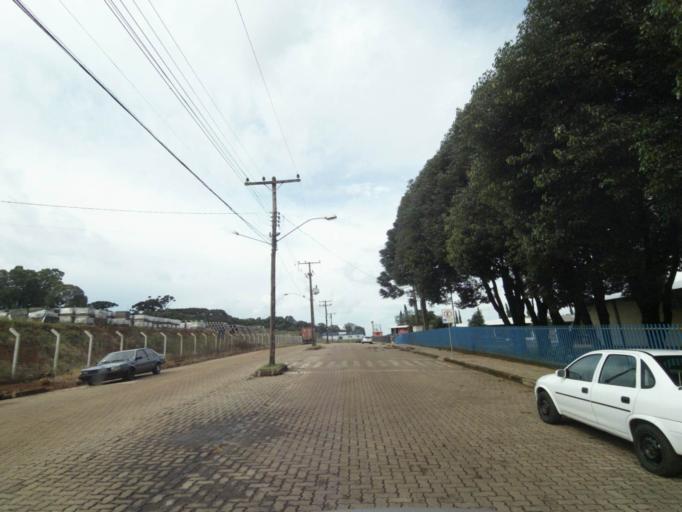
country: BR
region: Rio Grande do Sul
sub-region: Lagoa Vermelha
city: Lagoa Vermelha
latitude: -28.2272
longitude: -51.5093
